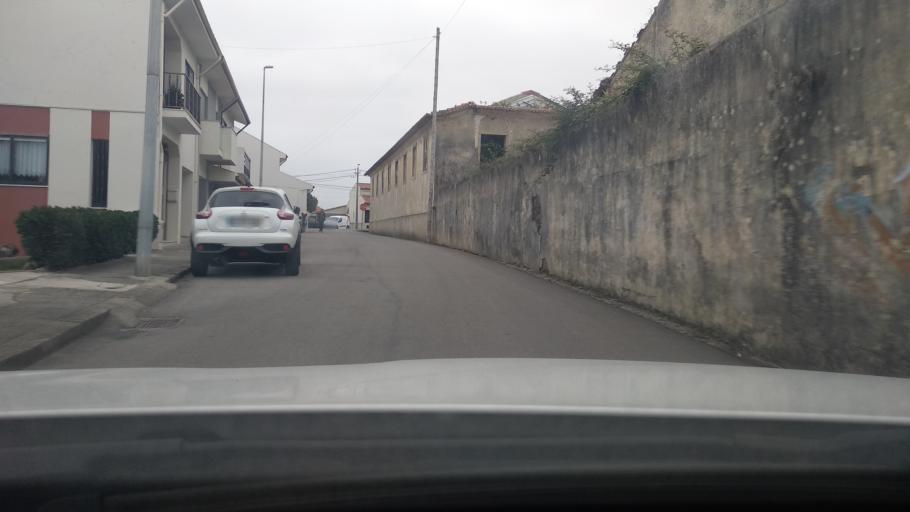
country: PT
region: Aveiro
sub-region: Espinho
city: Silvalde
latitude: 40.9893
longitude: -8.6360
